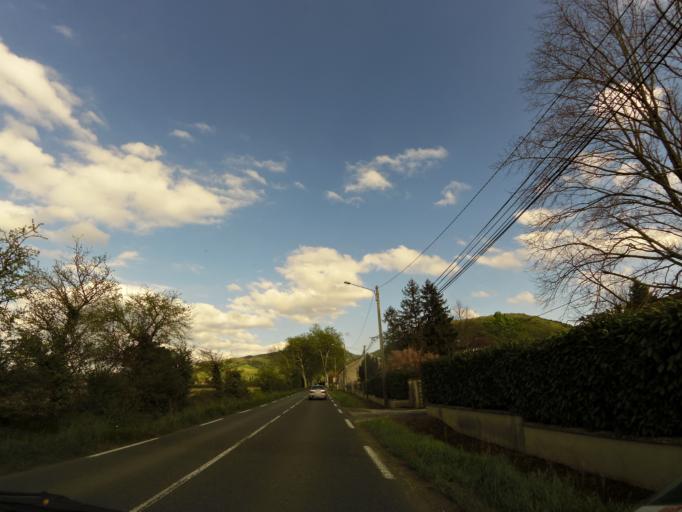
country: FR
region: Midi-Pyrenees
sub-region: Departement du Tarn
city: Soreze
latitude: 43.4506
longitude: 2.0569
